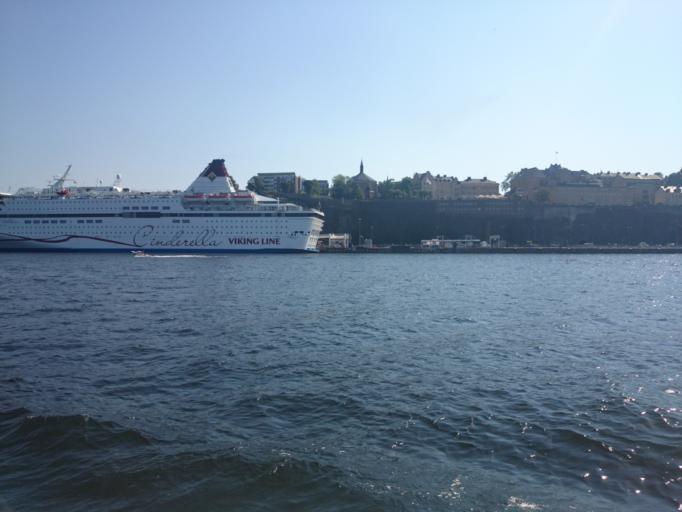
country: SE
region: Stockholm
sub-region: Stockholms Kommun
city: OEstermalm
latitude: 59.3198
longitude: 18.0930
